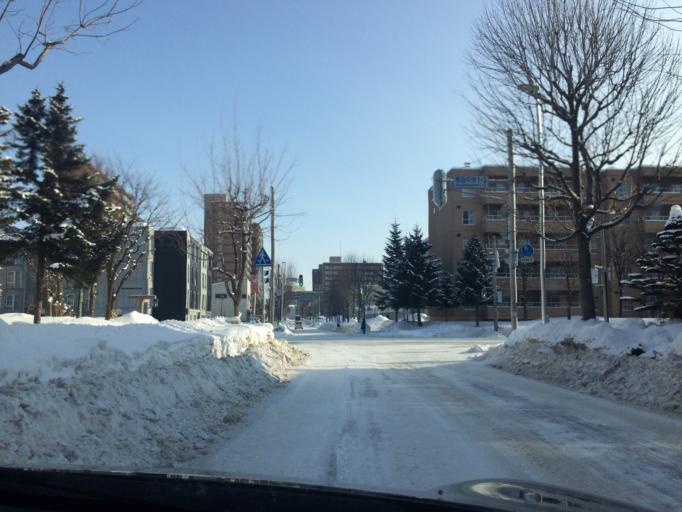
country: JP
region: Hokkaido
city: Ebetsu
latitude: 43.0343
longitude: 141.4651
